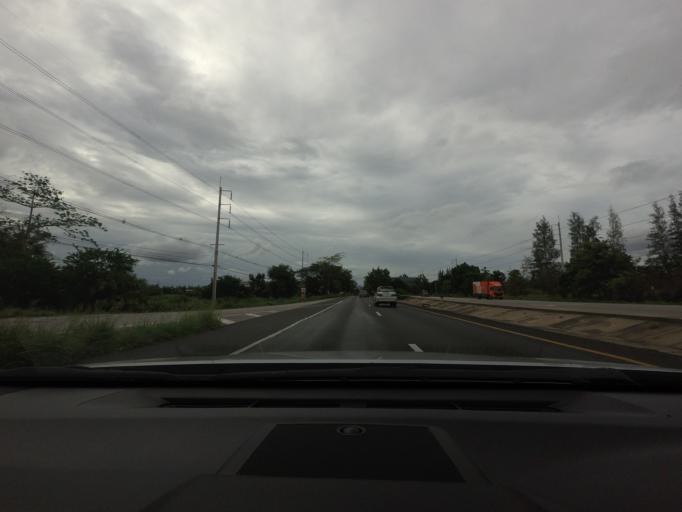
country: TH
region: Prachuap Khiri Khan
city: Hua Hin
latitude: 12.6239
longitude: 99.8583
